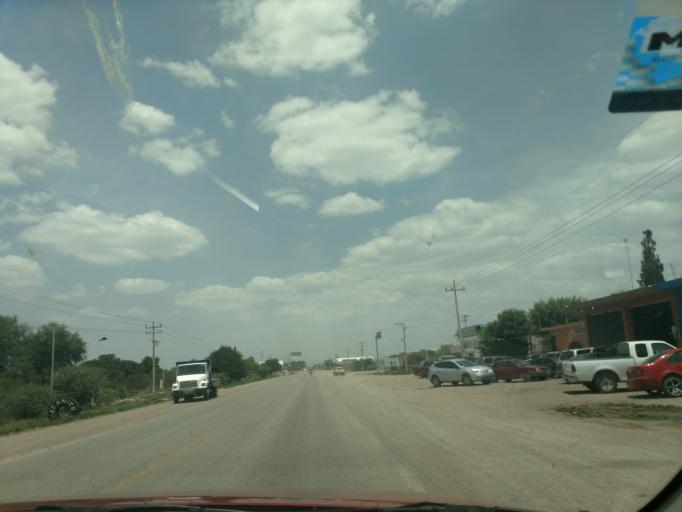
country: MX
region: San Luis Potosi
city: Ciudad Fernandez
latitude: 21.9465
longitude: -100.0536
